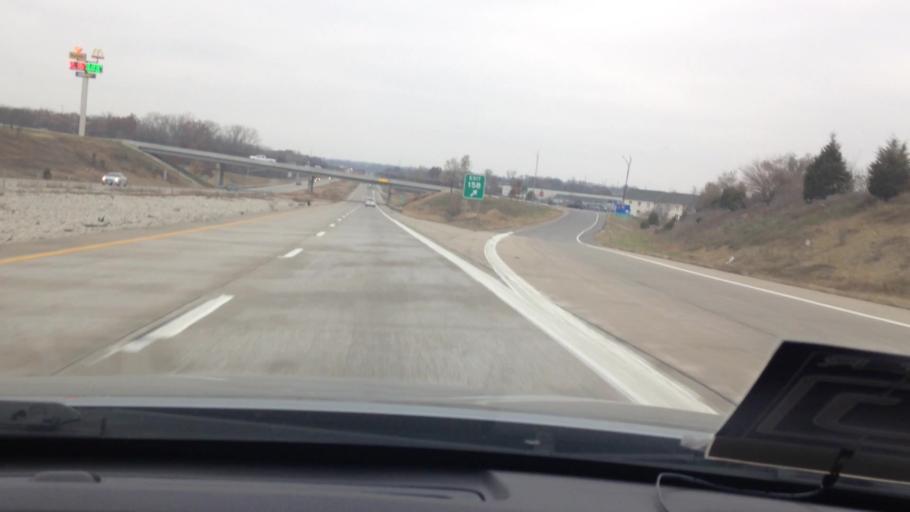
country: US
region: Missouri
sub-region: Cass County
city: Harrisonville
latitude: 38.6352
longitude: -94.3523
